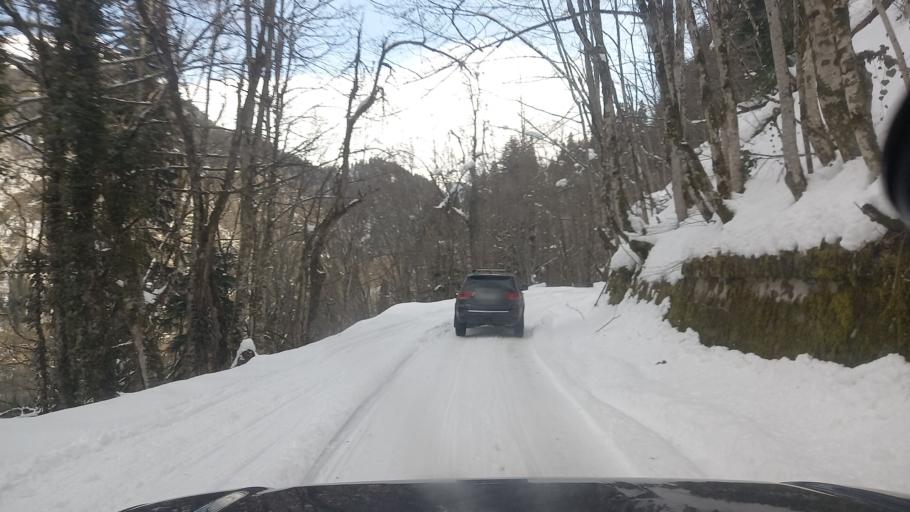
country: GE
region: Abkhazia
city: Gagra
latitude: 43.4781
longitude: 40.5449
